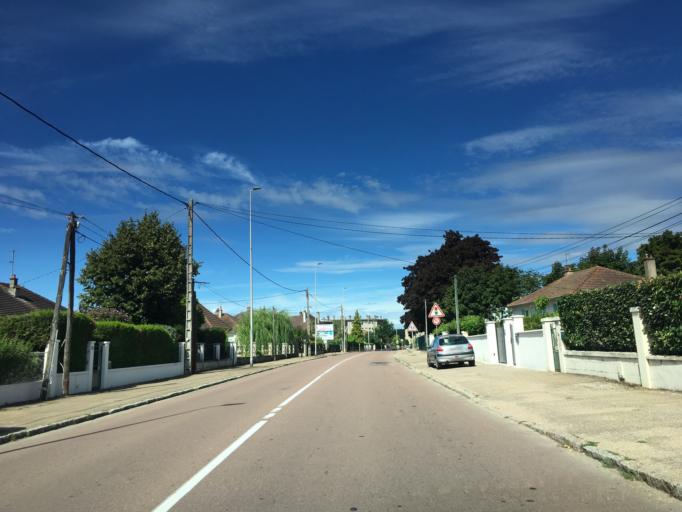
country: FR
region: Bourgogne
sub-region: Departement de l'Yonne
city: Auxerre
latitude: 47.7906
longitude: 3.5531
